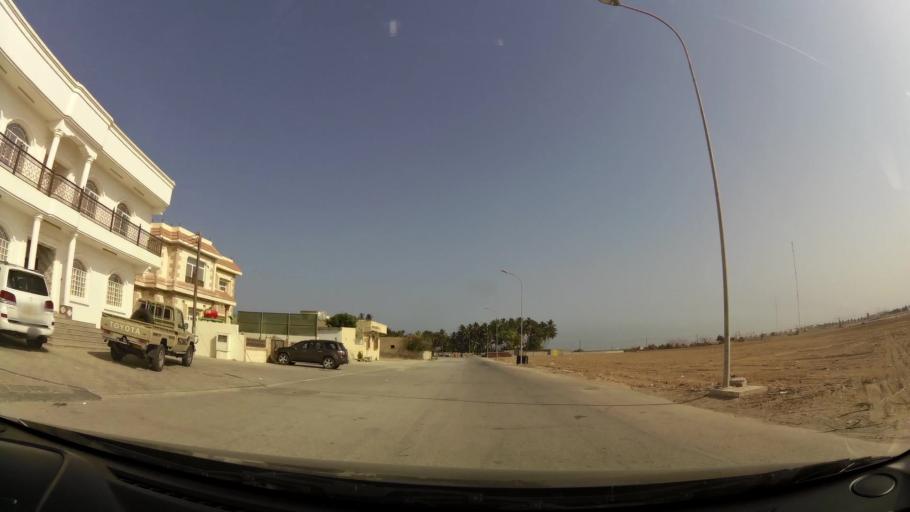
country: OM
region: Zufar
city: Salalah
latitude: 16.9984
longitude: 54.0359
